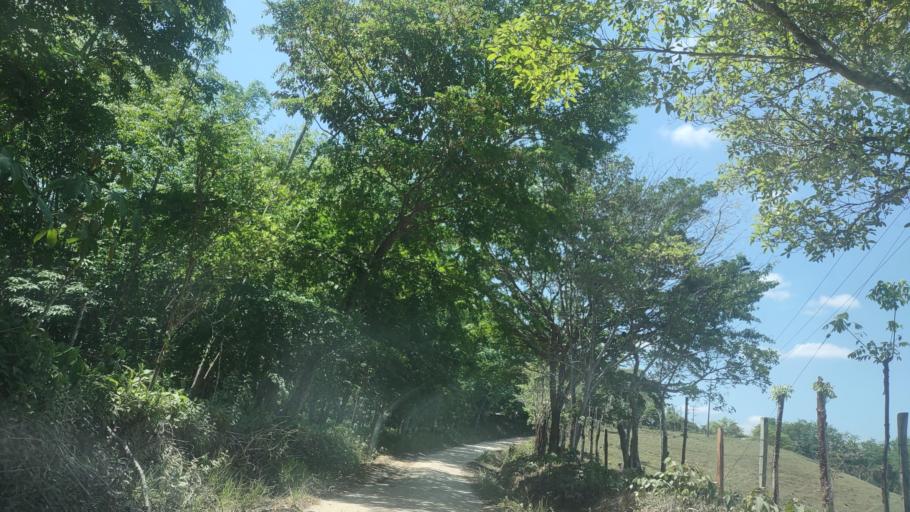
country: MX
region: Veracruz
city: Las Choapas
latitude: 17.7906
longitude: -94.1509
